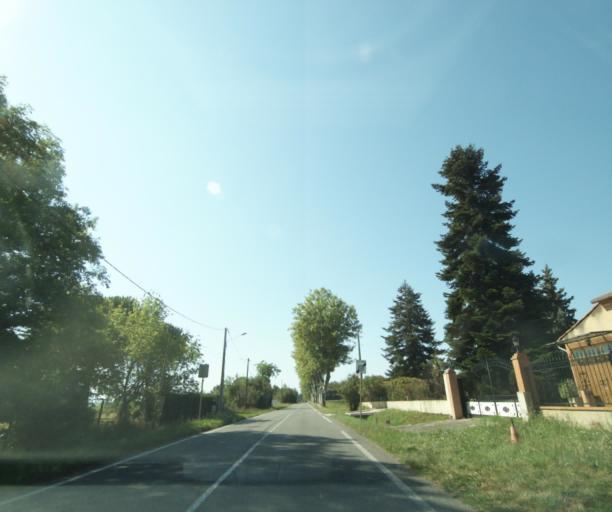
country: FR
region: Midi-Pyrenees
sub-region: Departement de la Haute-Garonne
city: Saint-Sulpice-sur-Leze
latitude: 43.3235
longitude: 1.3225
